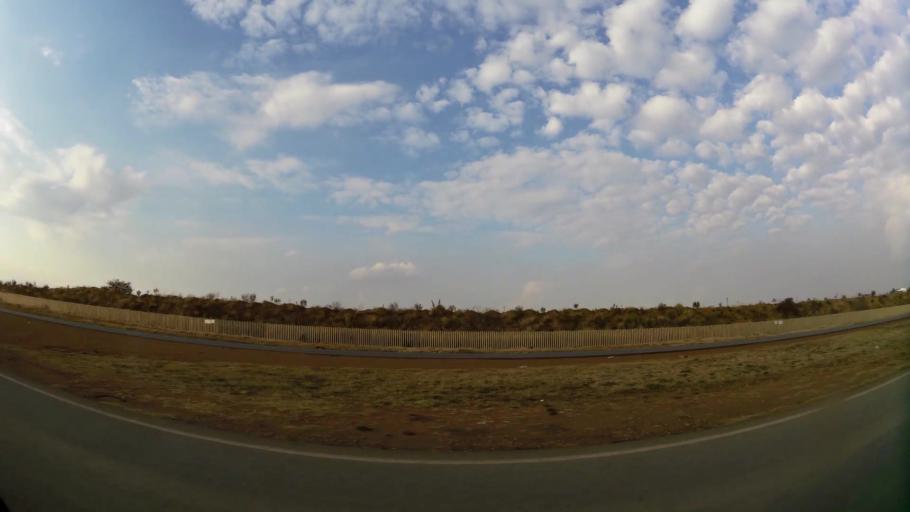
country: ZA
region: Gauteng
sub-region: Sedibeng District Municipality
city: Vereeniging
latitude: -26.6416
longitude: 27.8733
